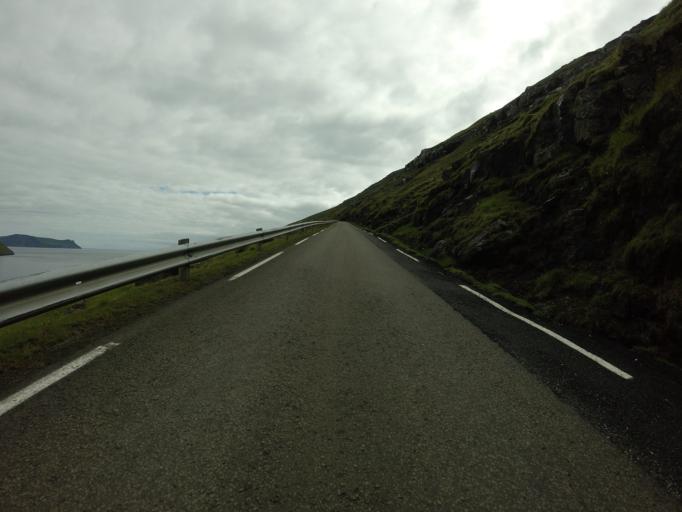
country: FO
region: Suduroy
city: Tvoroyri
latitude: 61.6242
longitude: -6.9359
